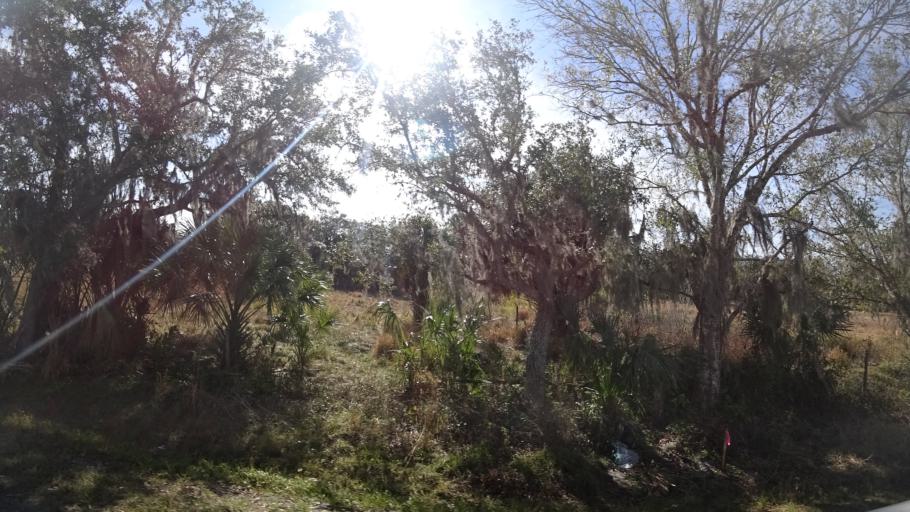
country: US
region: Florida
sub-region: Manatee County
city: Ellenton
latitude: 27.5822
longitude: -82.4471
